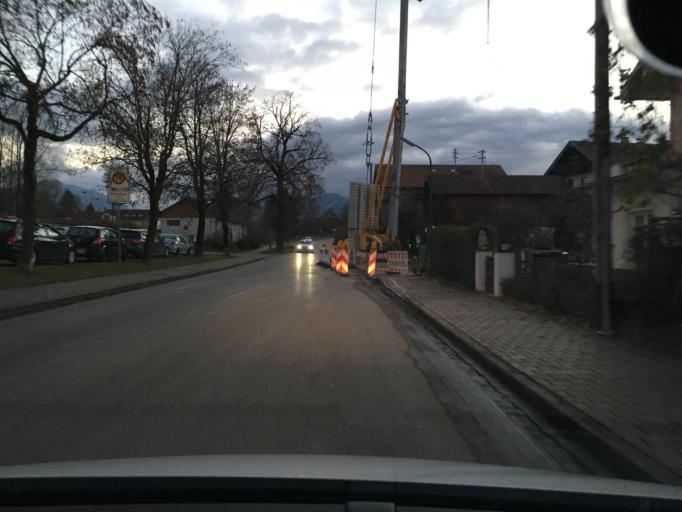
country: DE
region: Bavaria
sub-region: Upper Bavaria
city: Raubling
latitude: 47.7868
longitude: 12.1085
